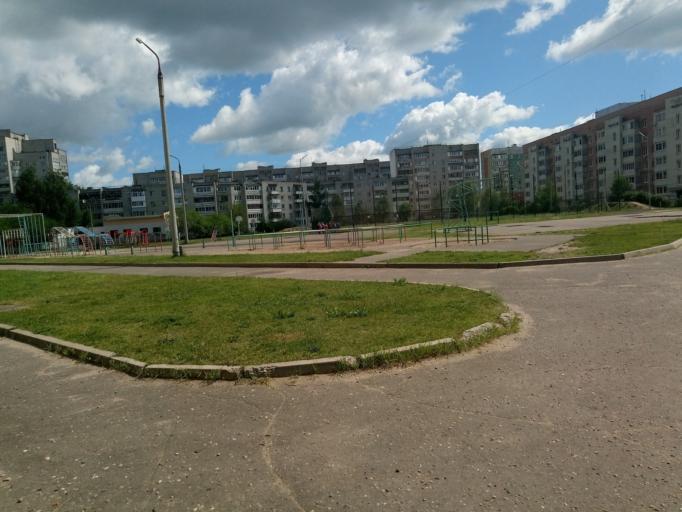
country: RU
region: Jaroslavl
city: Yaroslavl
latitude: 57.6418
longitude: 39.9534
